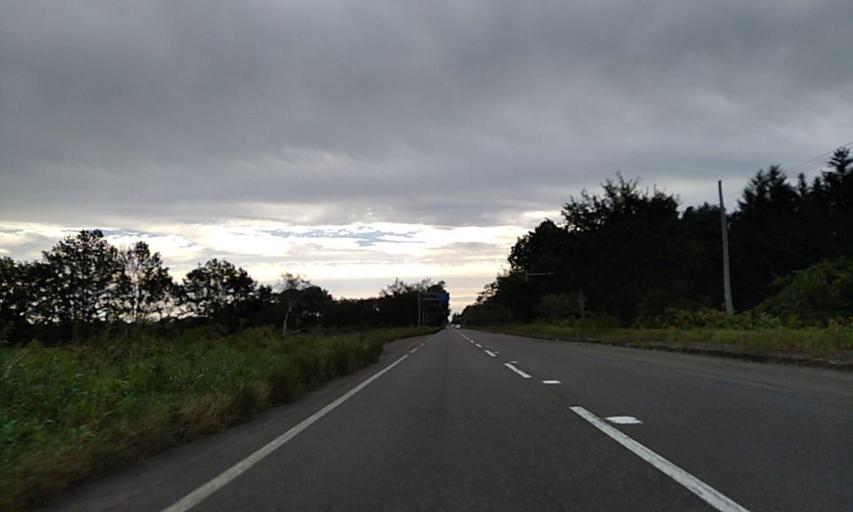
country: JP
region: Hokkaido
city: Otofuke
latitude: 42.9615
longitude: 142.9021
